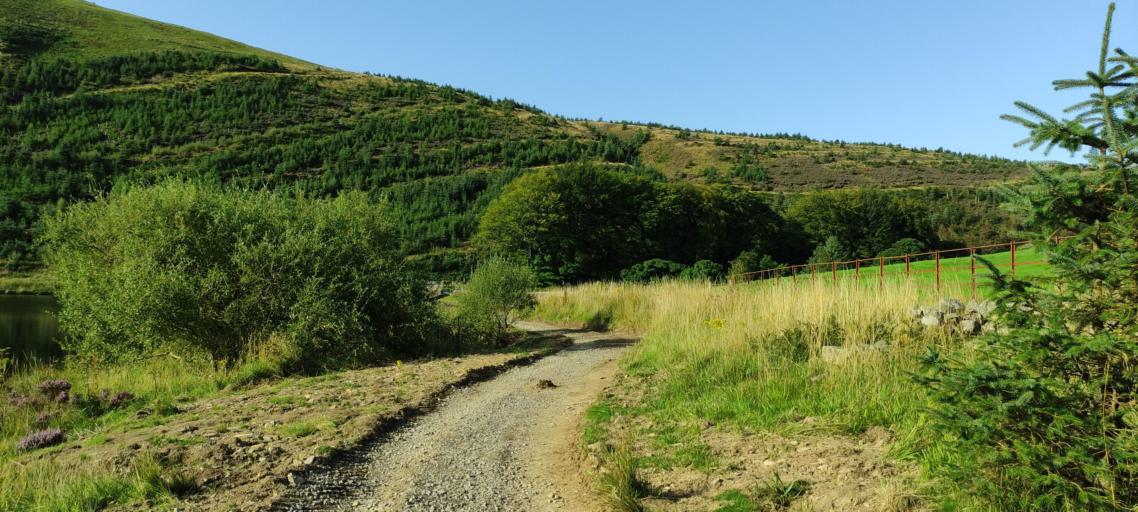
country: GB
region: England
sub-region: Cumbria
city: Frizington
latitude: 54.5639
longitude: -3.4042
